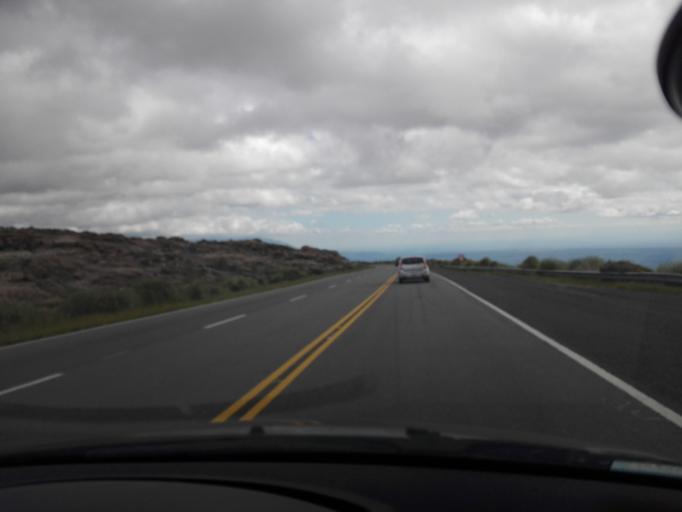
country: AR
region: Cordoba
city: Villa Cura Brochero
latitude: -31.6150
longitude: -64.9099
